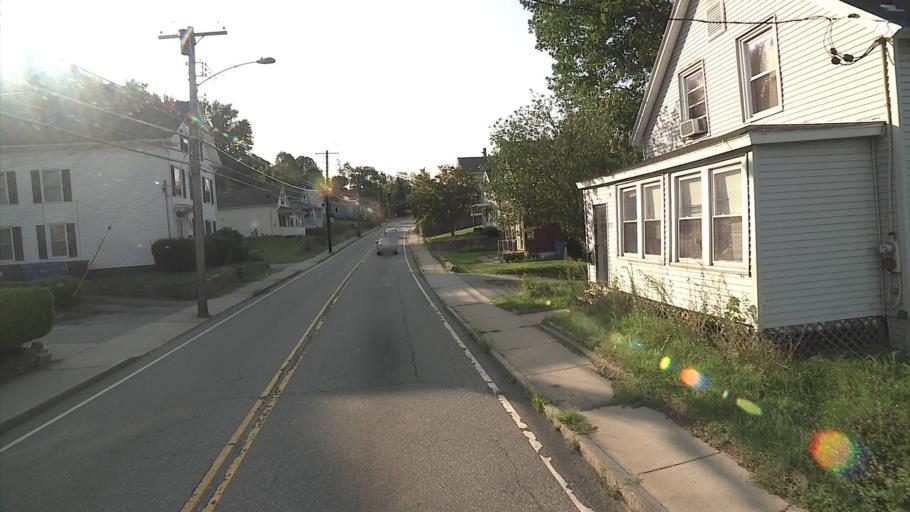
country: US
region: Connecticut
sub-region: New London County
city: Norwich
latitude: 41.5214
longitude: -72.0603
